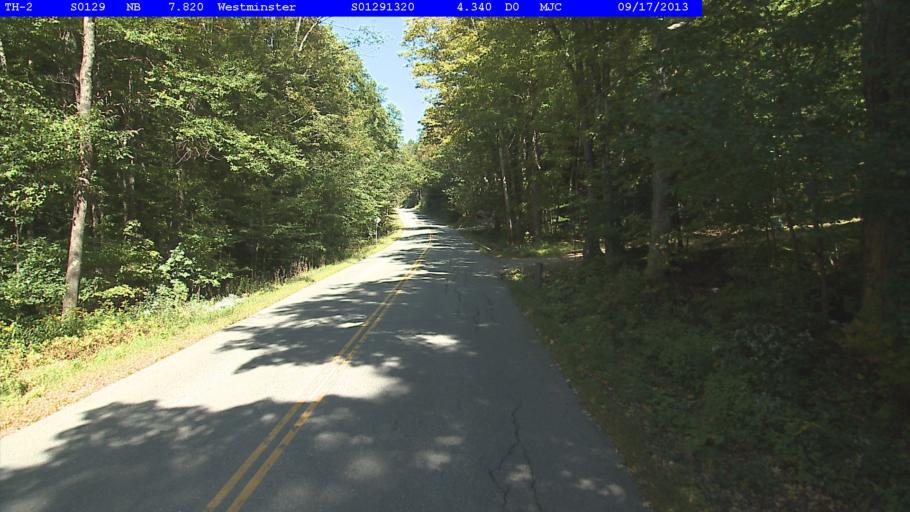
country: US
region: Vermont
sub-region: Windham County
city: Bellows Falls
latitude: 43.0777
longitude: -72.5374
